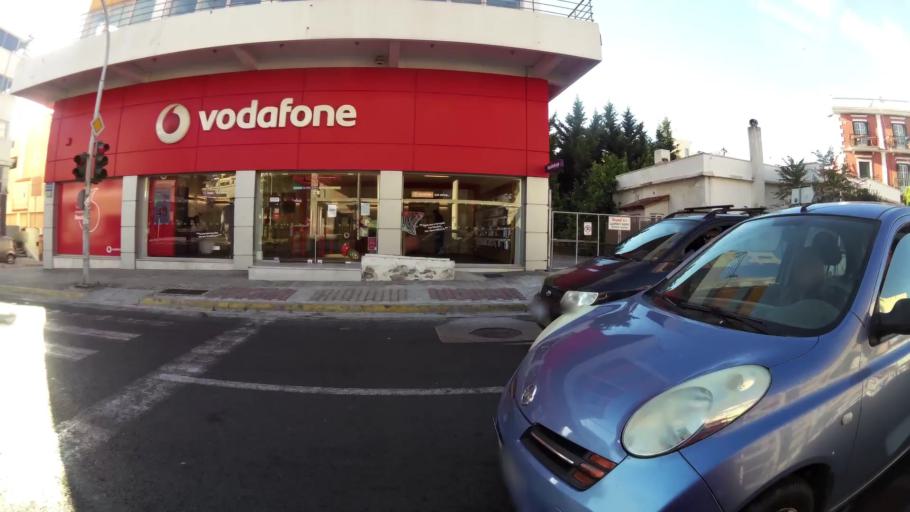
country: GR
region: Attica
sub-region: Nomarchia Anatolikis Attikis
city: Pallini
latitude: 38.0035
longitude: 23.8844
